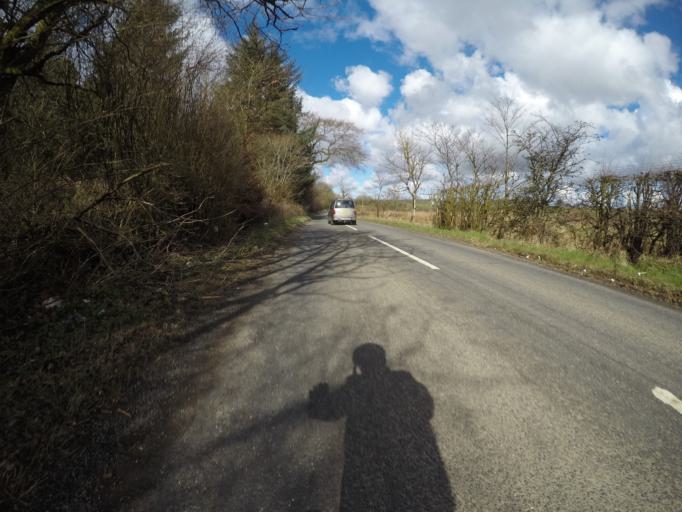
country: GB
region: Scotland
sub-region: North Ayrshire
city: Beith
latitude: 55.7334
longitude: -4.6136
